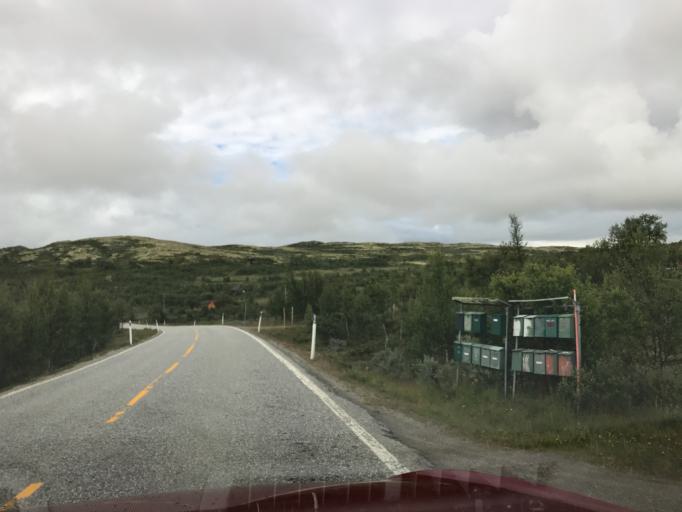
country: NO
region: Buskerud
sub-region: Al
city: Al
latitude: 60.3652
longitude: 8.4885
